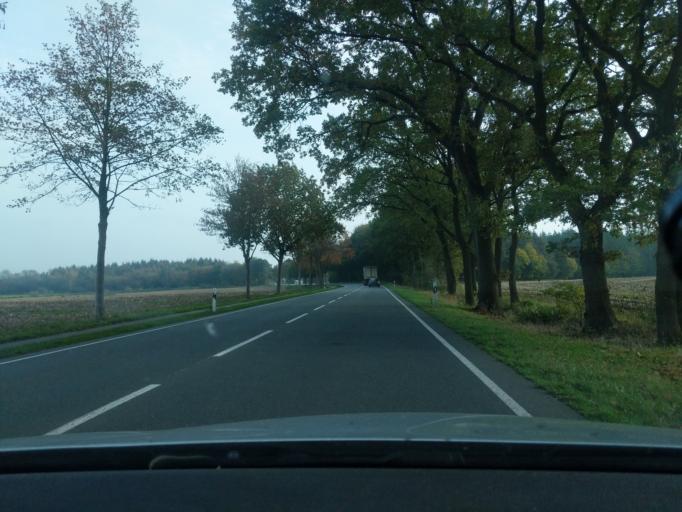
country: DE
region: Lower Saxony
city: Burweg
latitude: 53.6152
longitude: 9.2795
